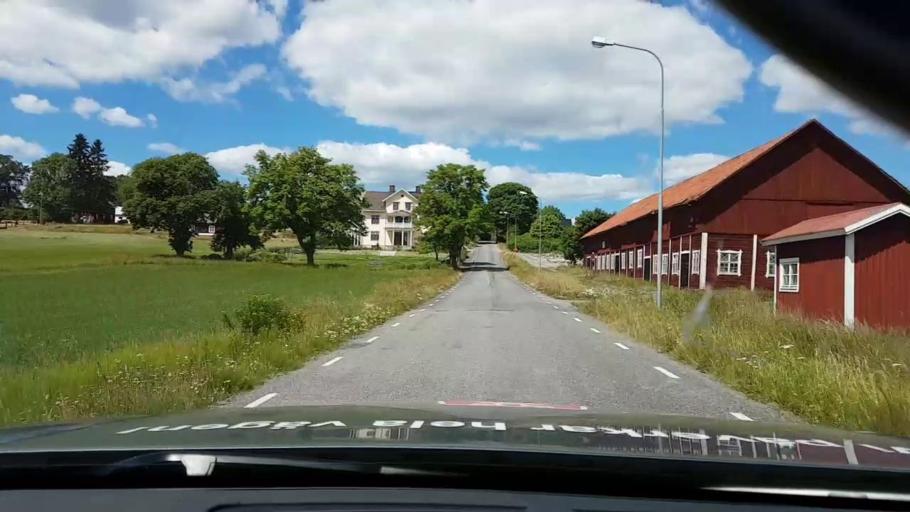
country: SE
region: Kalmar
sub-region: Vasterviks Kommun
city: Forserum
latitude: 58.0074
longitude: 16.5815
